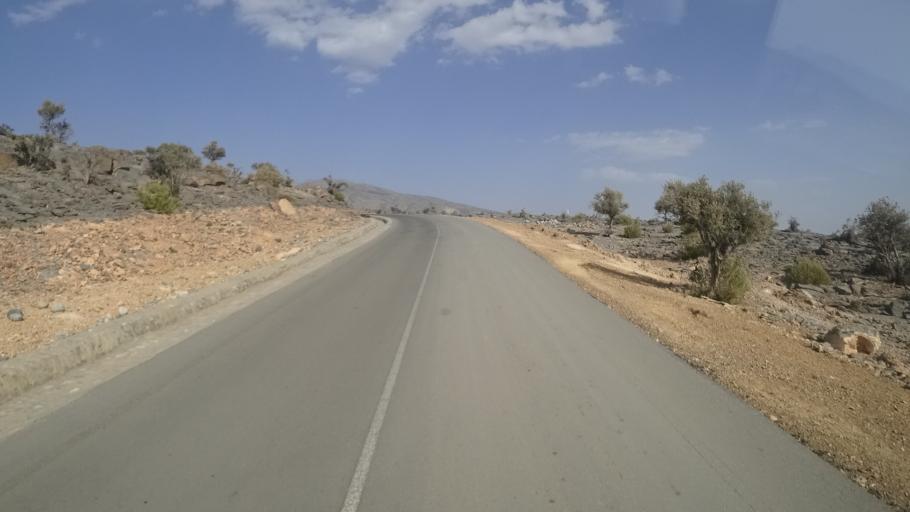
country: OM
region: Muhafazat ad Dakhiliyah
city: Bahla'
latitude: 23.2092
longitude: 57.2002
